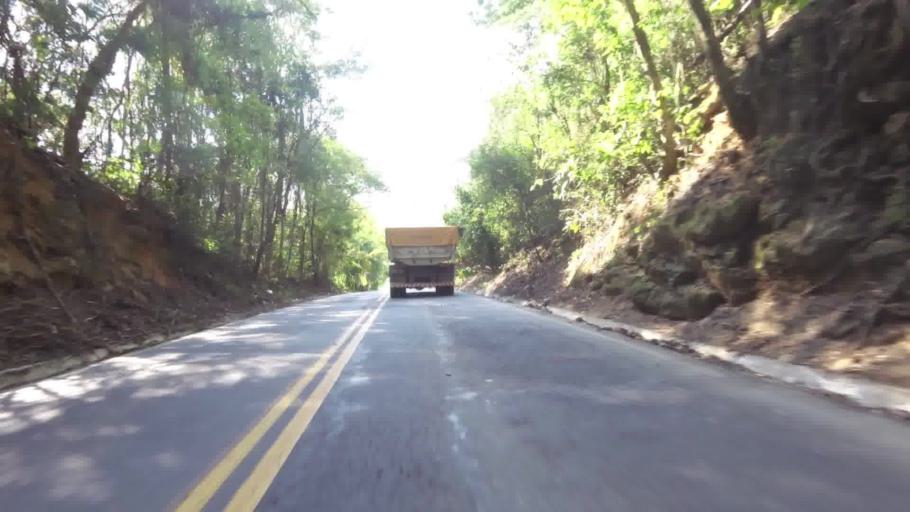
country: BR
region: Espirito Santo
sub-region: Rio Novo Do Sul
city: Rio Novo do Sul
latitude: -20.8691
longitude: -40.9070
